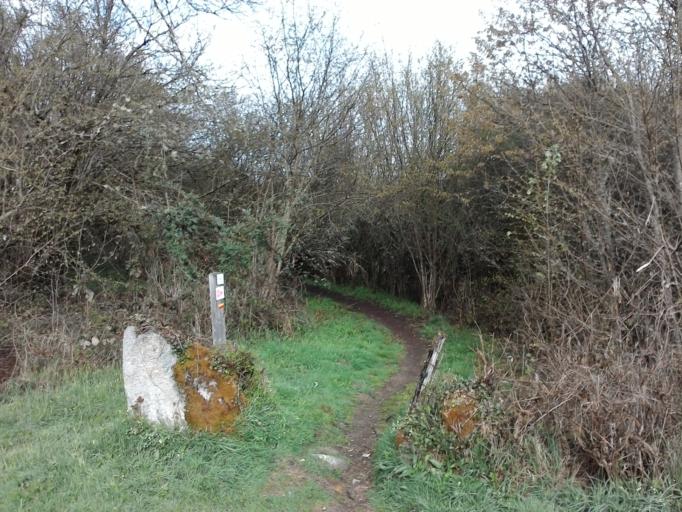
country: FR
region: Bourgogne
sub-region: Departement de la Cote-d'Or
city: Saulieu
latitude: 47.2499
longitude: 4.2064
